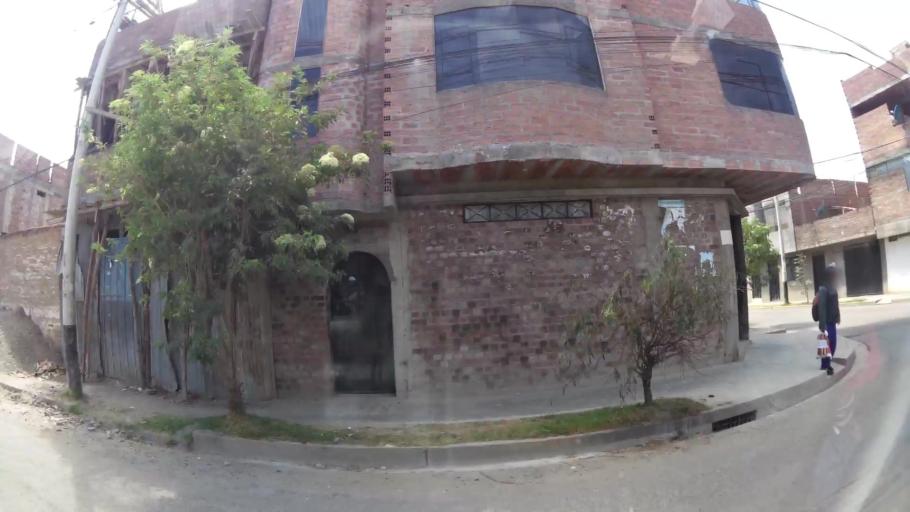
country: PE
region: Junin
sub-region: Provincia de Huancayo
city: El Tambo
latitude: -12.0757
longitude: -75.2179
